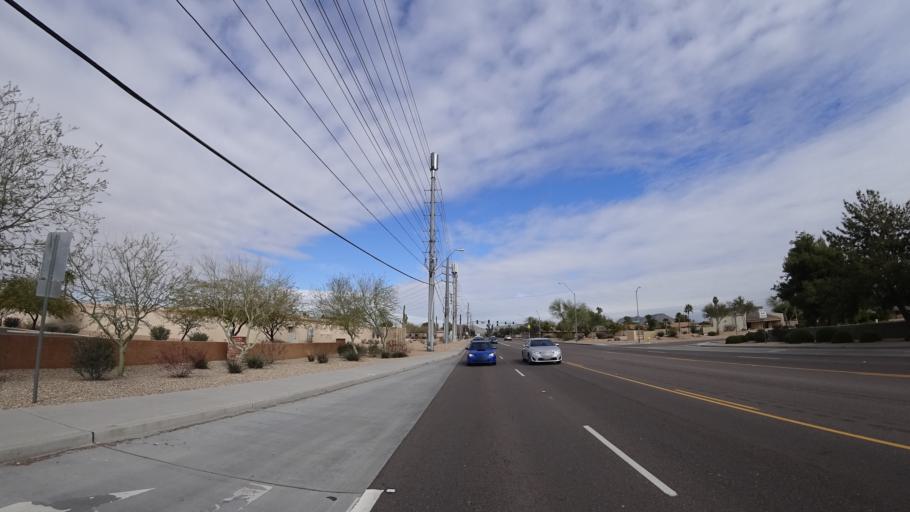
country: US
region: Arizona
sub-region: Maricopa County
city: Peoria
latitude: 33.6424
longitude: -112.1866
